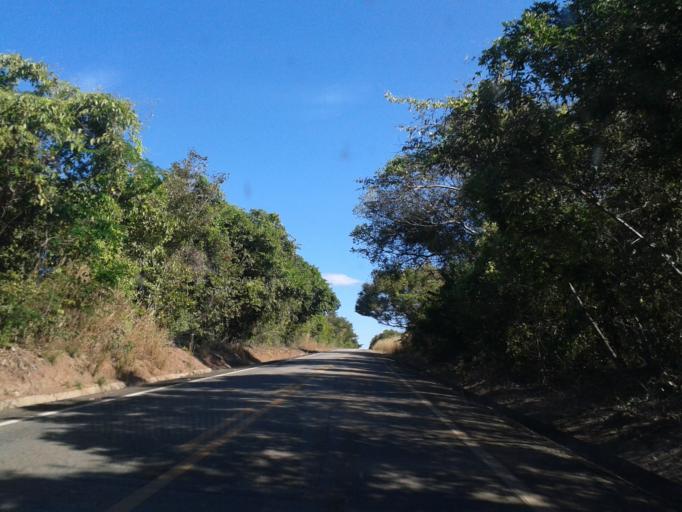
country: BR
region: Goias
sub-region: Mozarlandia
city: Mozarlandia
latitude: -14.4316
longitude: -50.4549
